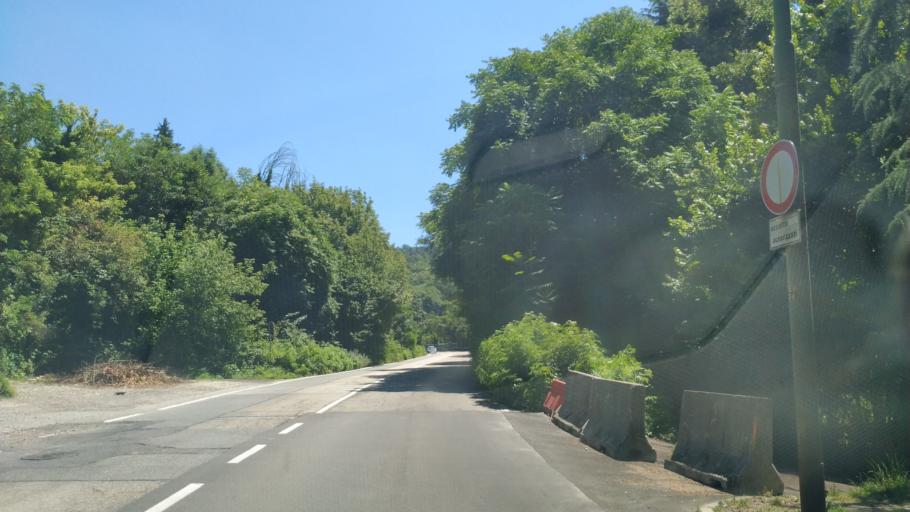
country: IT
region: Piedmont
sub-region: Provincia di Torino
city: San Mauro Torinese
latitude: 45.0778
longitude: 7.7393
